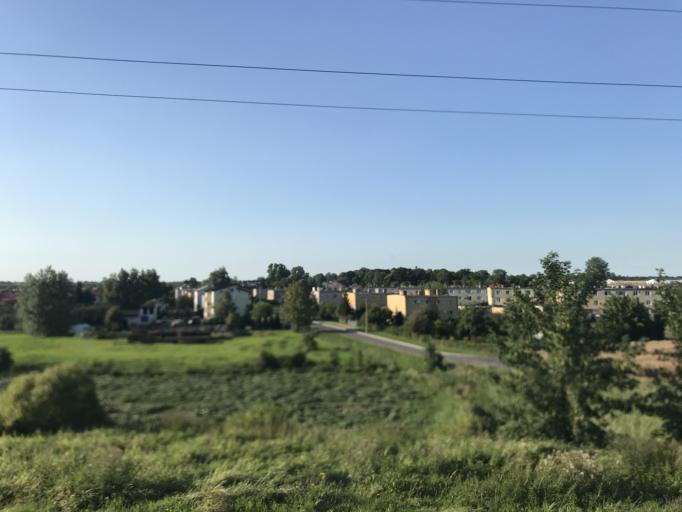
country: PL
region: Pomeranian Voivodeship
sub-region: Powiat malborski
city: Lisewo Malborskie
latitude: 54.0927
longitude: 18.8301
